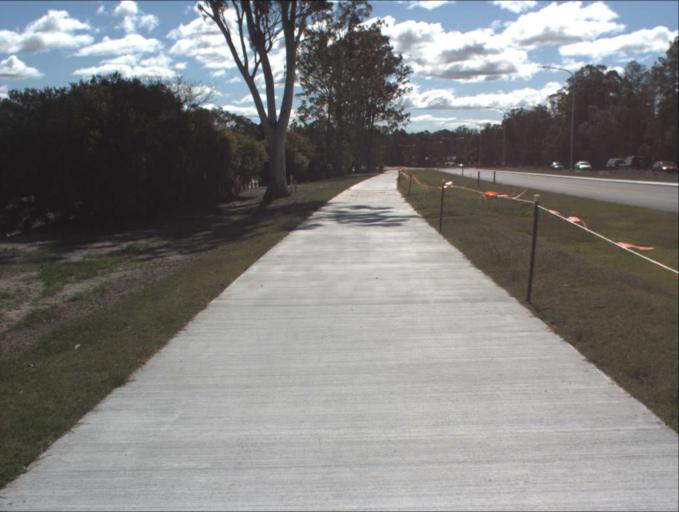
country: AU
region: Queensland
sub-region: Logan
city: Logan Reserve
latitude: -27.6985
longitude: 153.1002
